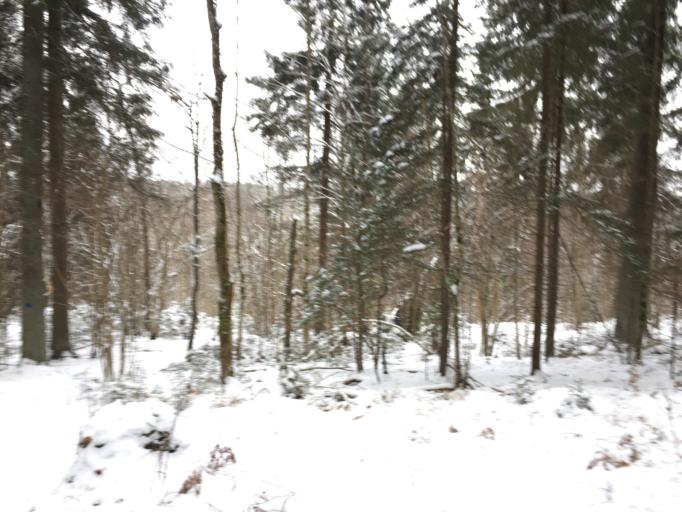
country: LV
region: Amatas Novads
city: Drabesi
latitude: 57.2240
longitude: 25.1711
